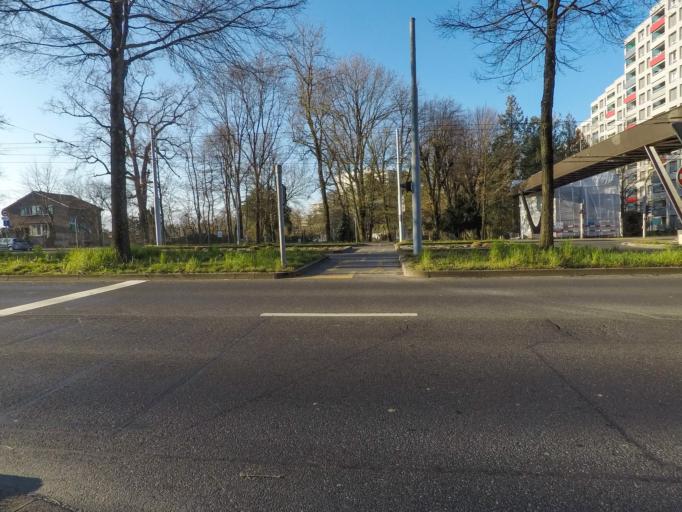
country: CH
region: Geneva
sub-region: Geneva
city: Les Avanchets
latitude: 46.2198
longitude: 6.1064
